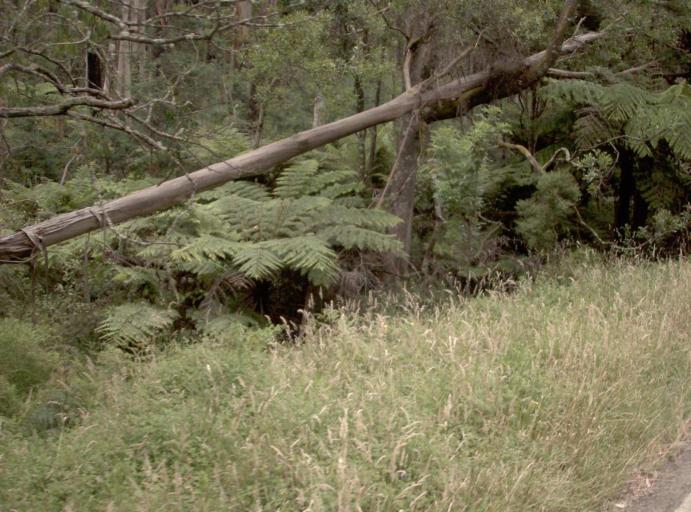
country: AU
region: Victoria
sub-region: Yarra Ranges
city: Healesville
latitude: -37.6149
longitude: 145.6035
